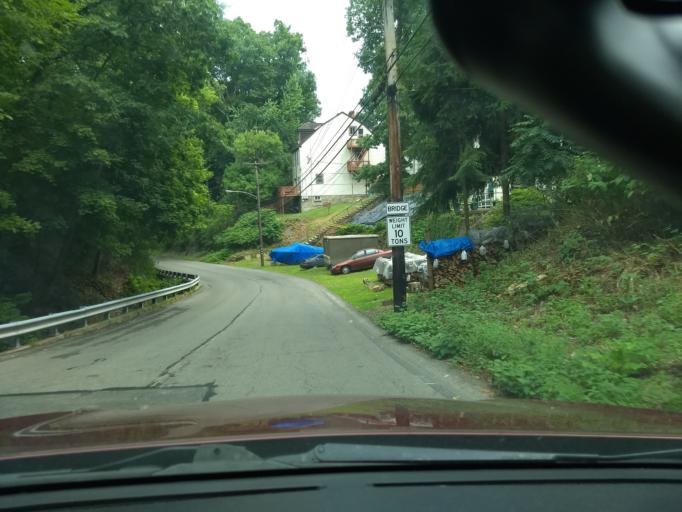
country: US
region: Pennsylvania
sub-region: Allegheny County
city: Bellevue
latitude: 40.4991
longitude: -80.0488
